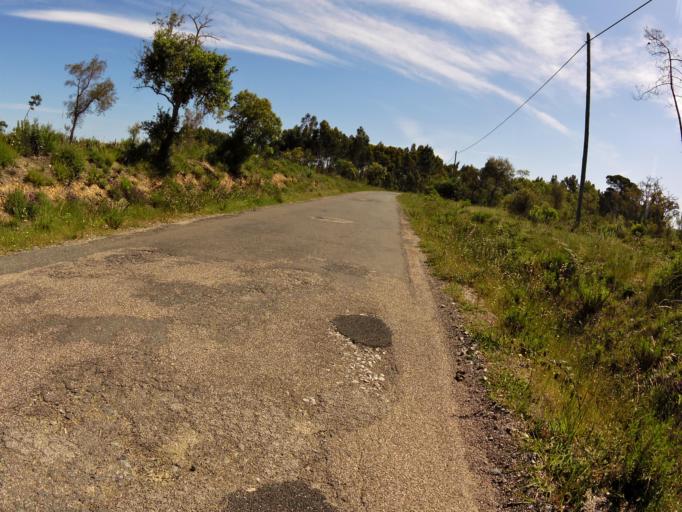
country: PT
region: Setubal
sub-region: Sines
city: Porto Covo
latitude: 37.9378
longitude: -8.7525
